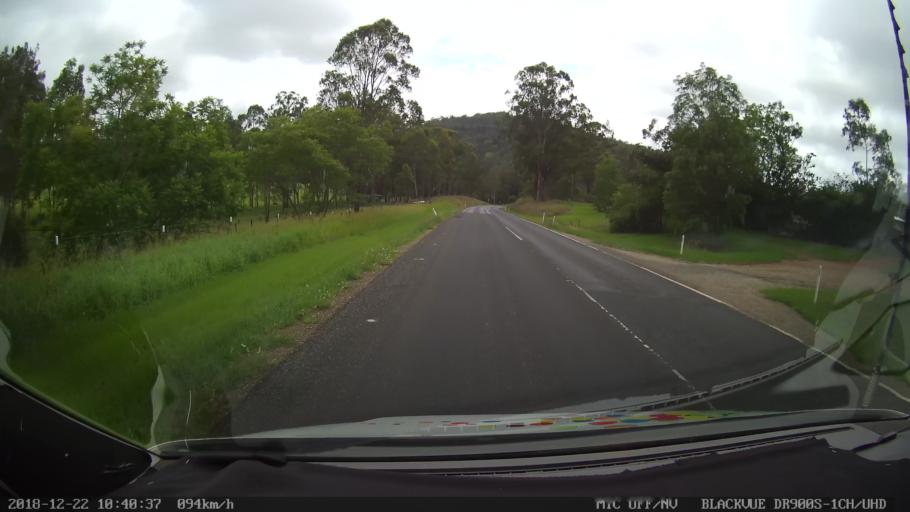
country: AU
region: New South Wales
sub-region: Clarence Valley
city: South Grafton
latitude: -29.6297
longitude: 152.7515
